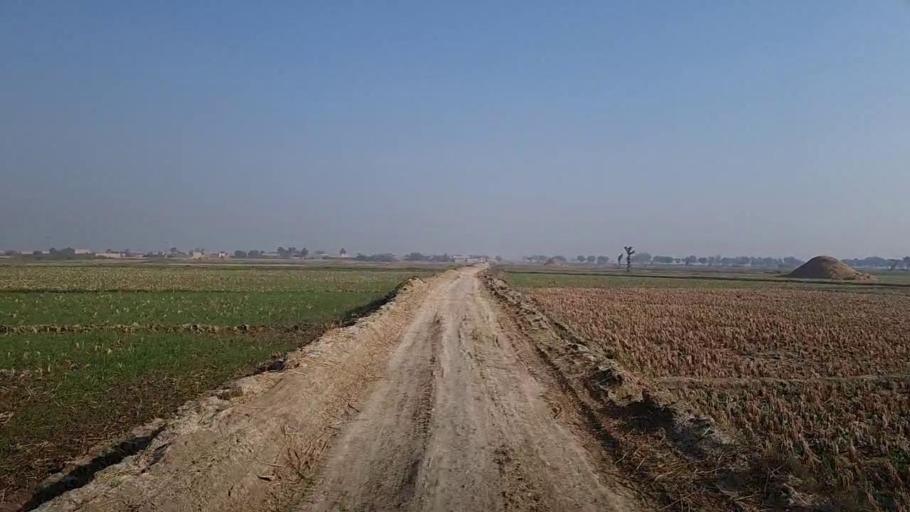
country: PK
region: Sindh
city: Radhan
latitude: 27.1135
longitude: 67.8935
